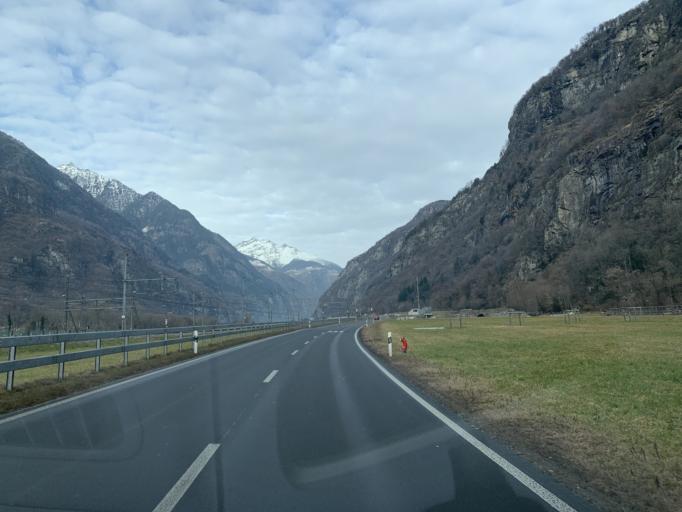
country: CH
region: Ticino
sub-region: Leventina District
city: Bodio
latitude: 46.3700
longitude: 8.9302
